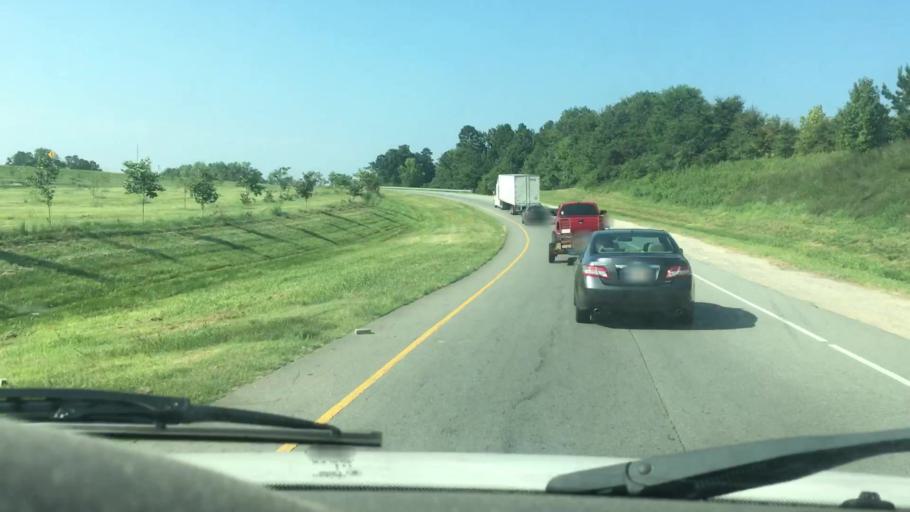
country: US
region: North Carolina
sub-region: Gaston County
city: Mount Holly
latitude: 35.3224
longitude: -80.9422
